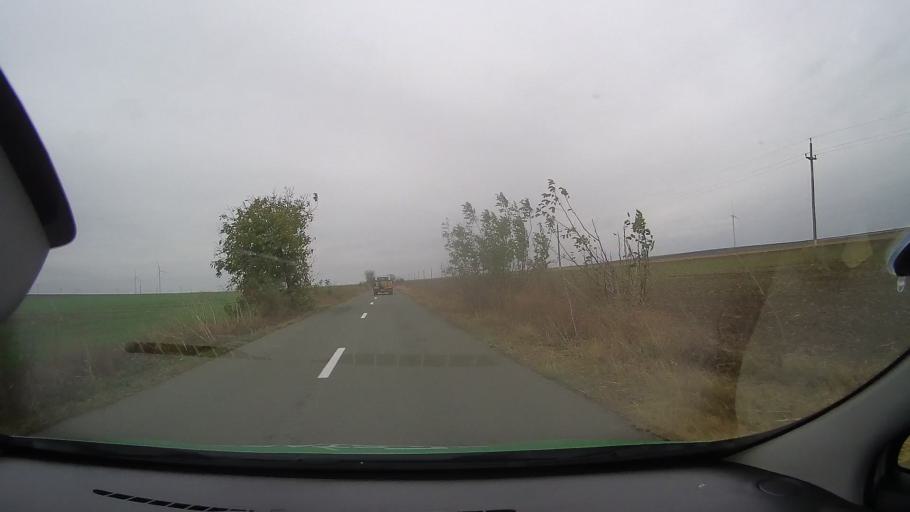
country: RO
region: Constanta
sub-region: Comuna Targusor
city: Targusor
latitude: 44.4725
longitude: 28.3851
